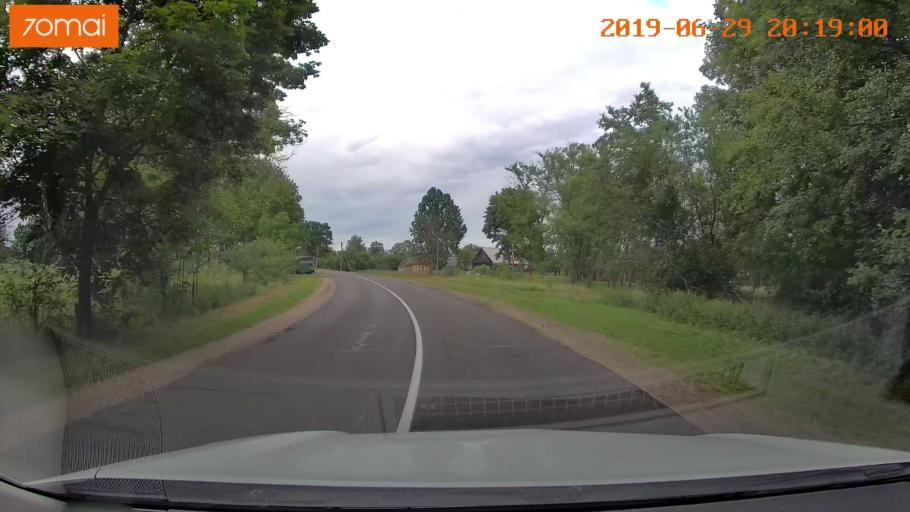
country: BY
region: Brest
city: Asnyezhytsy
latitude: 52.3973
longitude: 26.2426
